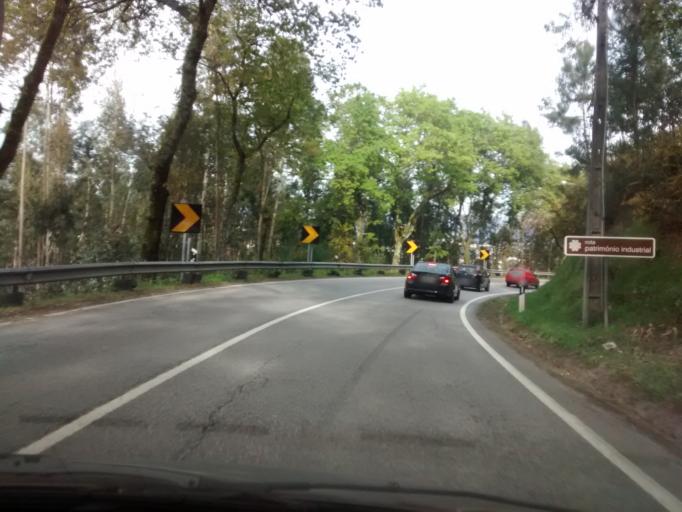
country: PT
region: Braga
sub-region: Guimaraes
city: Brito
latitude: 41.5039
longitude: -8.3822
